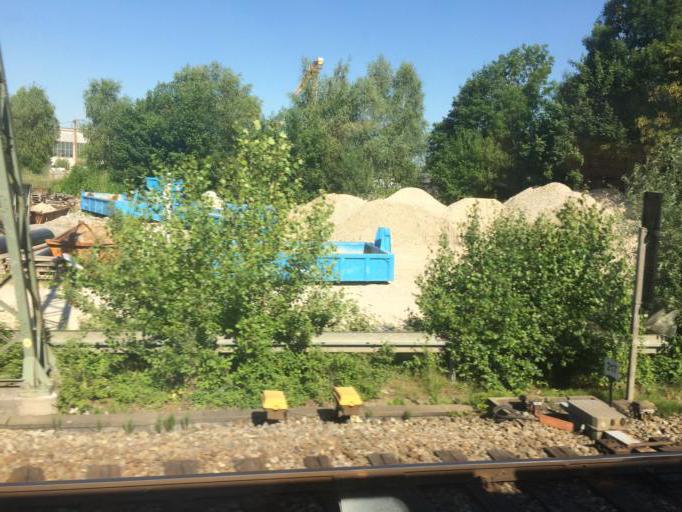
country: DE
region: Bavaria
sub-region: Upper Bavaria
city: Unterfoehring
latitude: 48.1751
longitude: 11.6452
